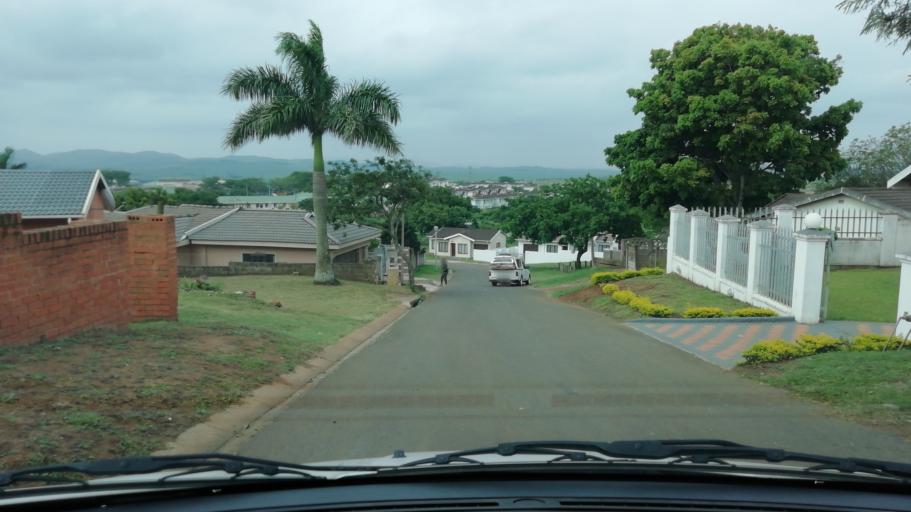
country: ZA
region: KwaZulu-Natal
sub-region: uThungulu District Municipality
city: Empangeni
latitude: -28.7375
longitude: 31.8782
